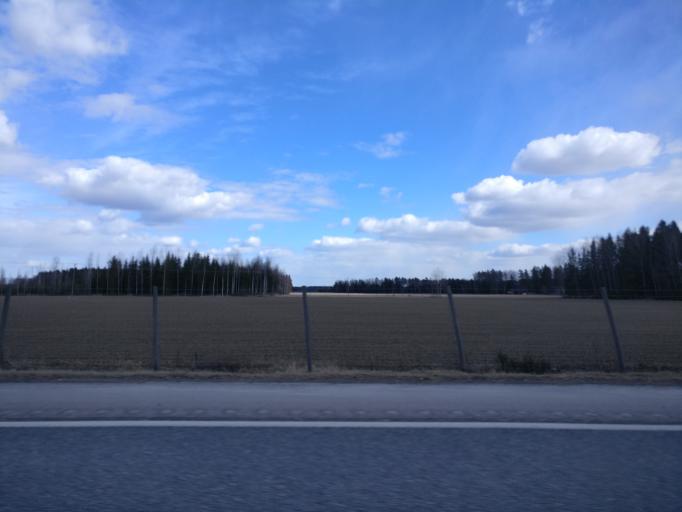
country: FI
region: Haeme
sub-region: Riihimaeki
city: Riihimaeki
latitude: 60.7675
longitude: 24.7194
